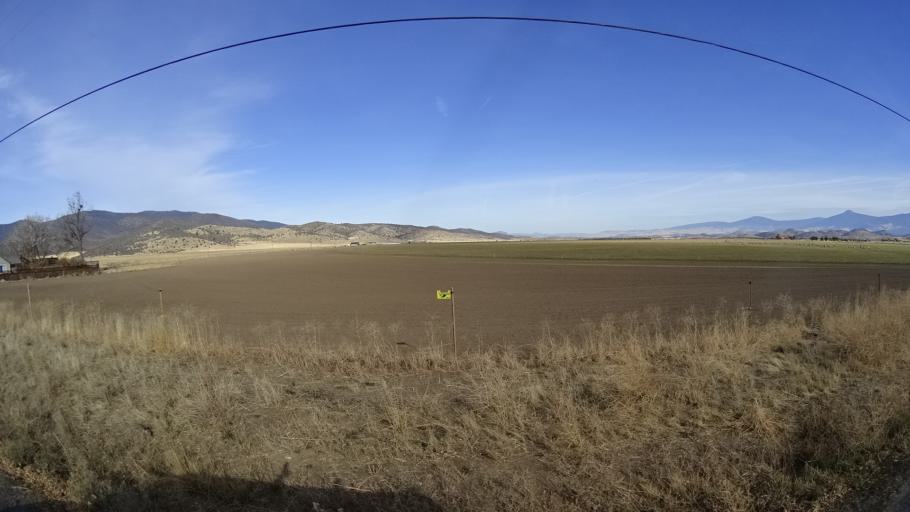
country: US
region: California
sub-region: Siskiyou County
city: Montague
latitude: 41.5383
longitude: -122.5607
